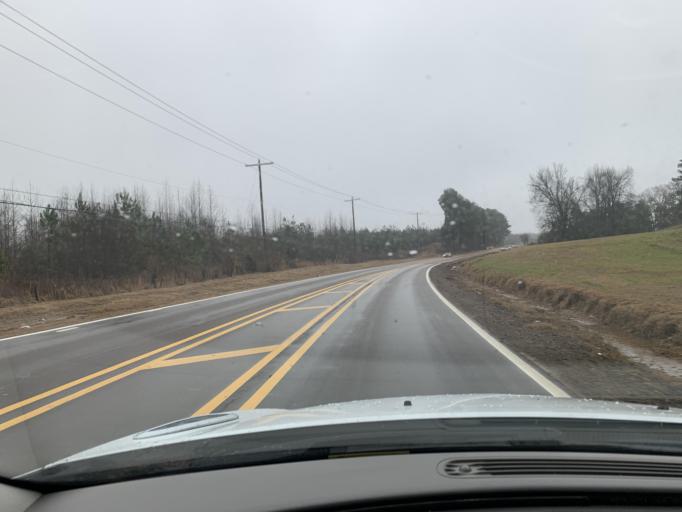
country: US
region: Mississippi
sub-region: De Soto County
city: Horn Lake
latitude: 34.9088
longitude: -89.9995
